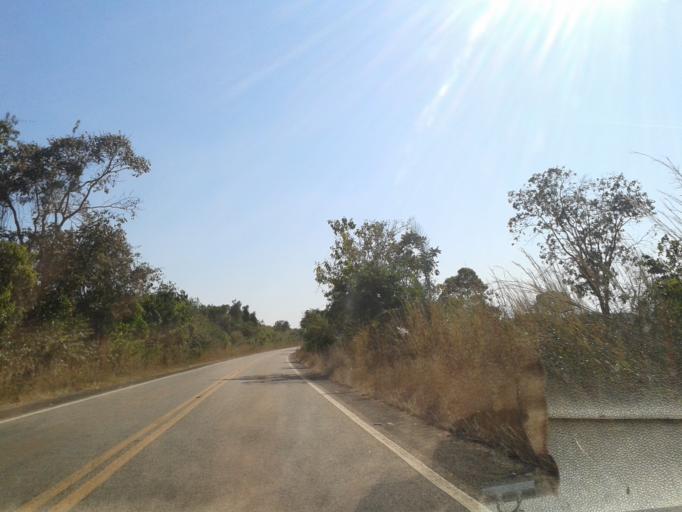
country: BR
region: Goias
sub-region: Mozarlandia
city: Mozarlandia
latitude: -14.6194
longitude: -50.5180
